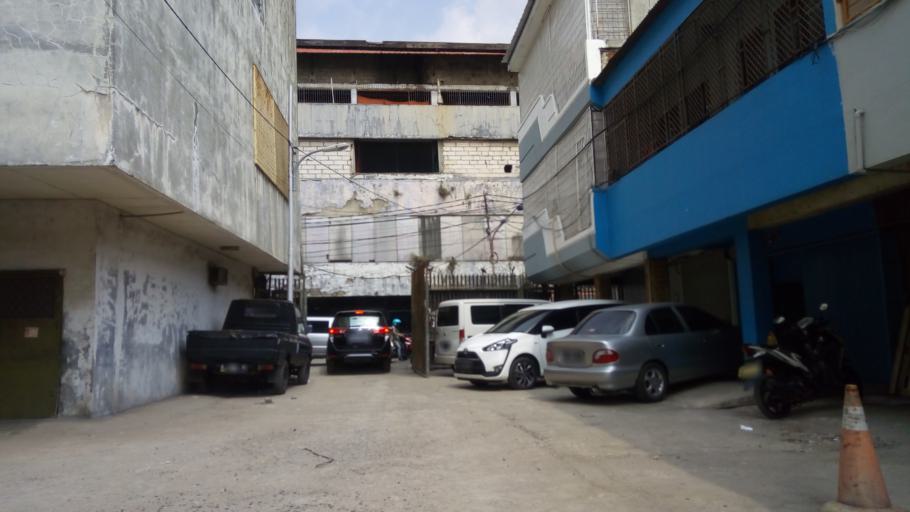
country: ID
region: Jakarta Raya
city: Jakarta
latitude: -6.1609
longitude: 106.8283
